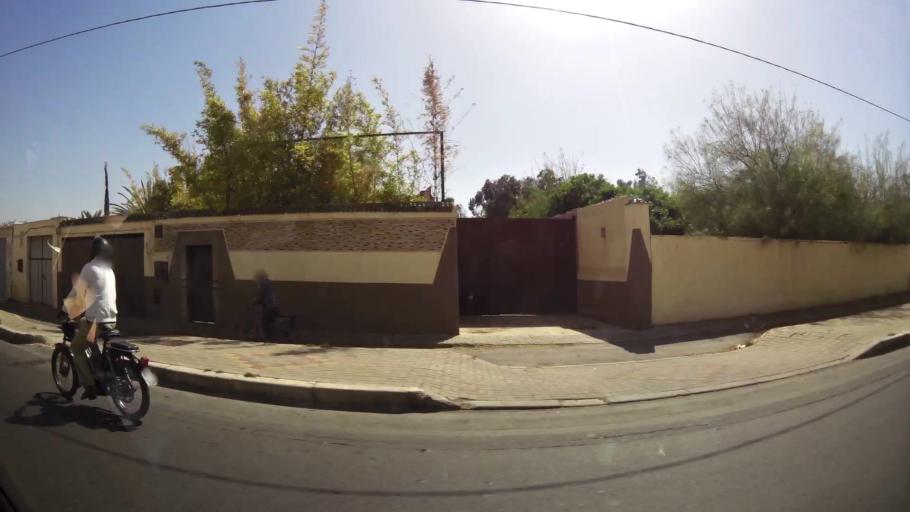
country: MA
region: Souss-Massa-Draa
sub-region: Inezgane-Ait Mellou
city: Inezgane
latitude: 30.3705
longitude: -9.5495
